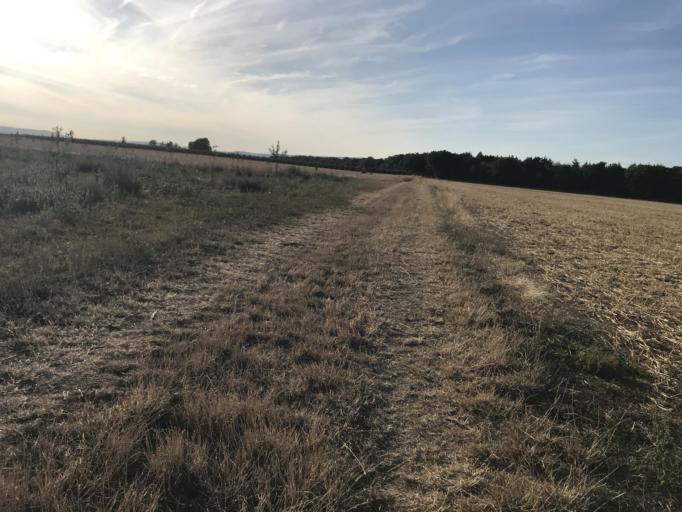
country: DE
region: Rheinland-Pfalz
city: Ober-Olm
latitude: 49.9465
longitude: 8.1794
